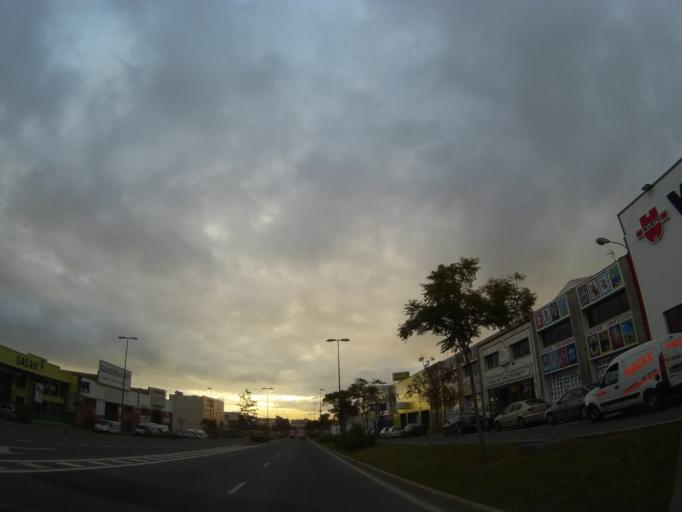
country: ES
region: Andalusia
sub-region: Provincia de Malaga
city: Malaga
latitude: 36.7071
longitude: -4.4742
